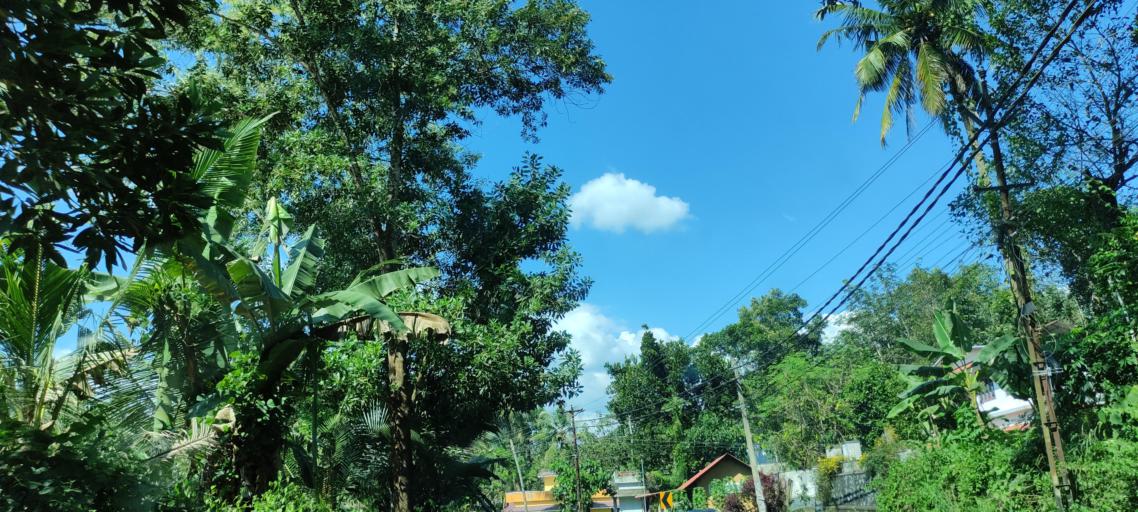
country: IN
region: Kerala
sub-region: Pattanamtitta
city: Adur
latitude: 9.1719
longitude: 76.7418
